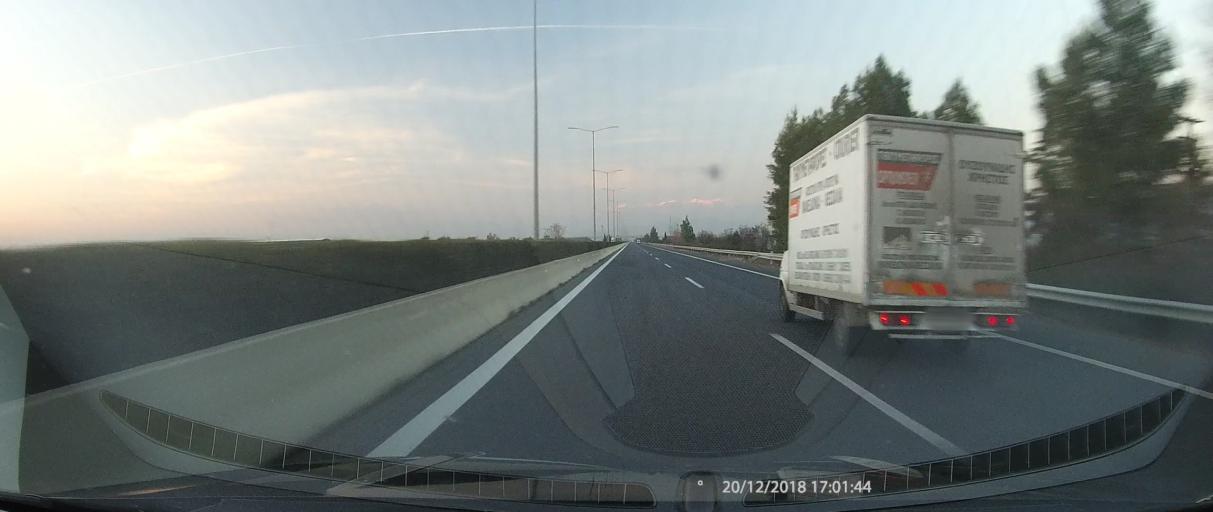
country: GR
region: Thessaly
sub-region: Nomos Larisis
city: Platykampos
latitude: 39.6613
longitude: 22.5046
